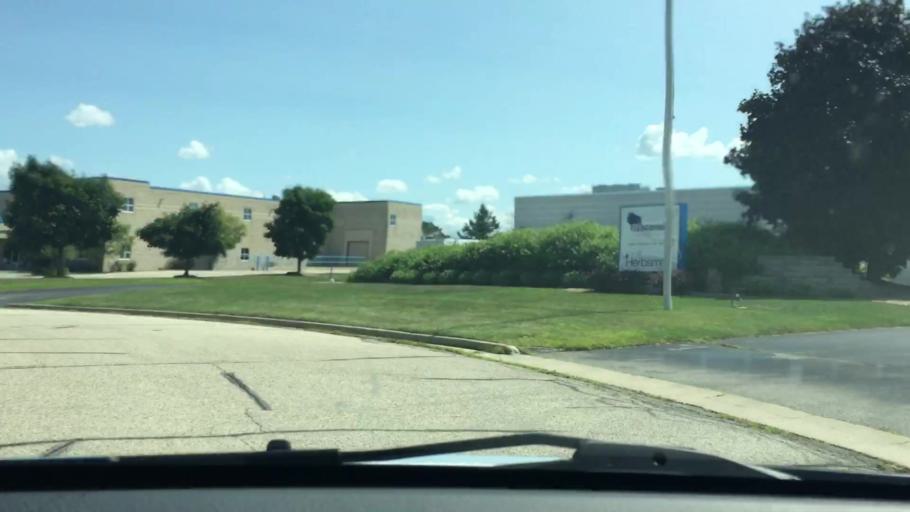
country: US
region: Wisconsin
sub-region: Waukesha County
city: Oconomowoc
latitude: 43.0736
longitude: -88.4755
